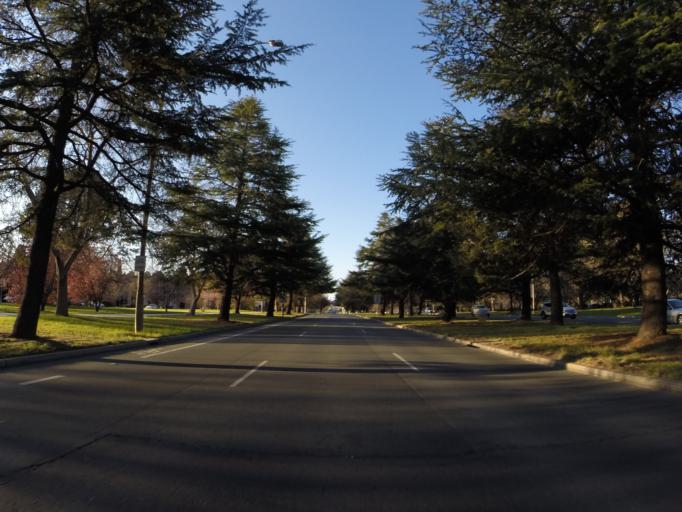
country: AU
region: Australian Capital Territory
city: Forrest
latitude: -35.2994
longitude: 149.1257
